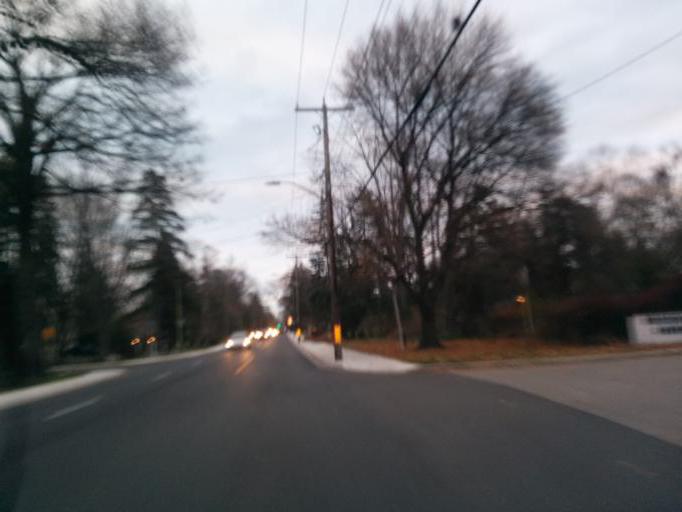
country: CA
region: Ontario
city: Mississauga
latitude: 43.5517
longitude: -79.6073
